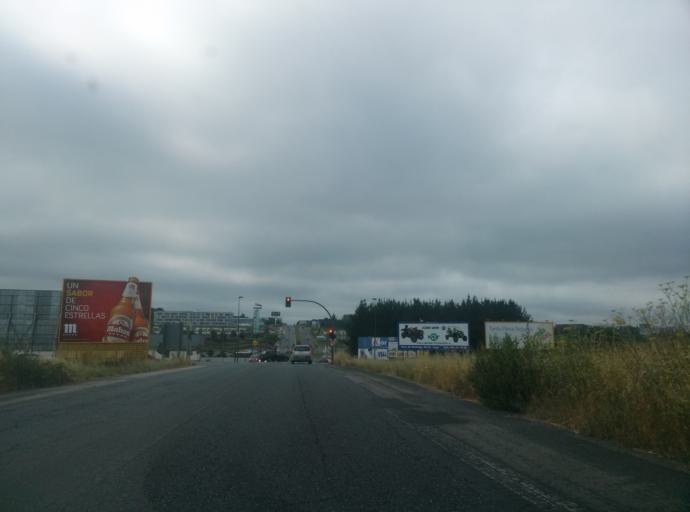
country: ES
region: Galicia
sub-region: Provincia de Lugo
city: Lugo
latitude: 43.0341
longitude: -7.5644
